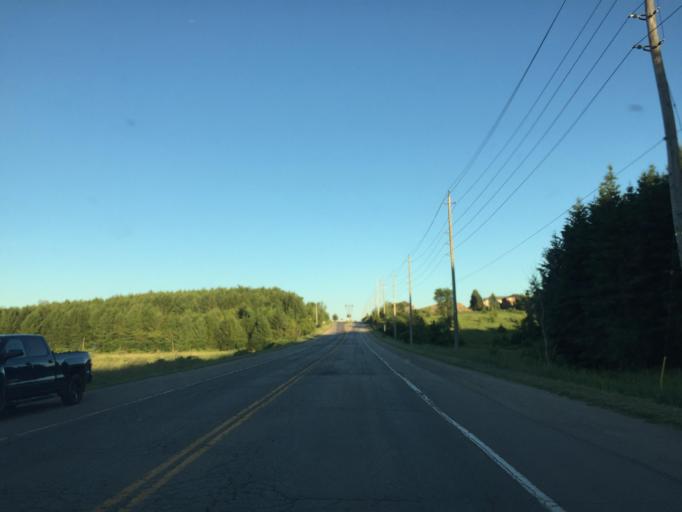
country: CA
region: Ontario
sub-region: Wellington County
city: Guelph
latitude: 43.5863
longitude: -80.2717
